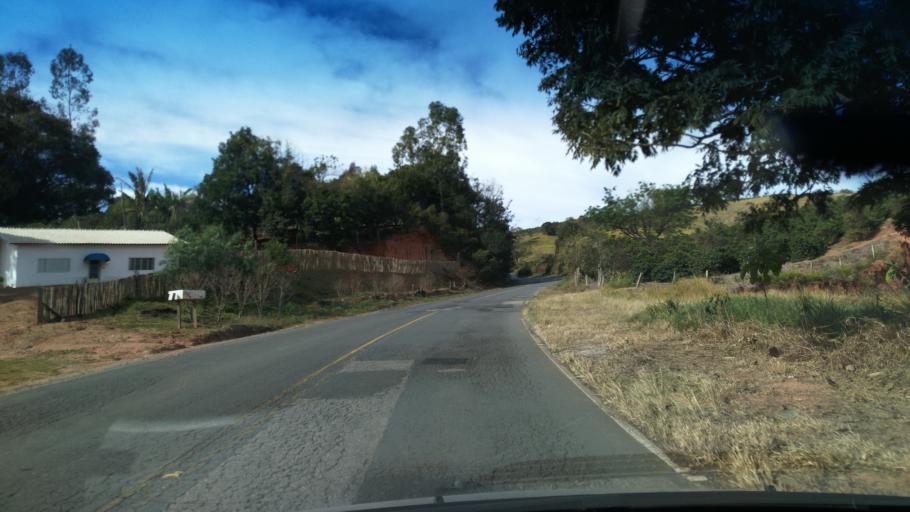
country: BR
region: Minas Gerais
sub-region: Andradas
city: Andradas
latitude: -22.0603
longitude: -46.3782
